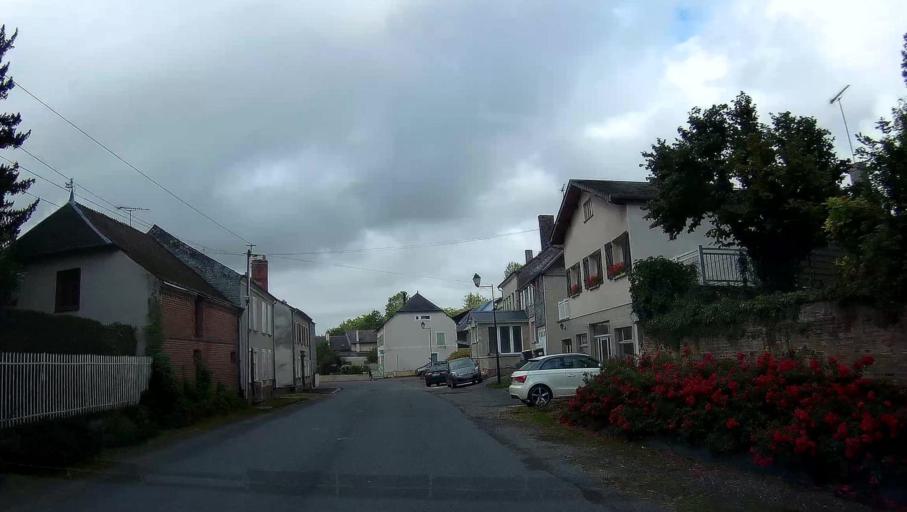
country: FR
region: Champagne-Ardenne
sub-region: Departement des Ardennes
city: Chateau-Porcien
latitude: 49.6507
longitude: 4.2484
